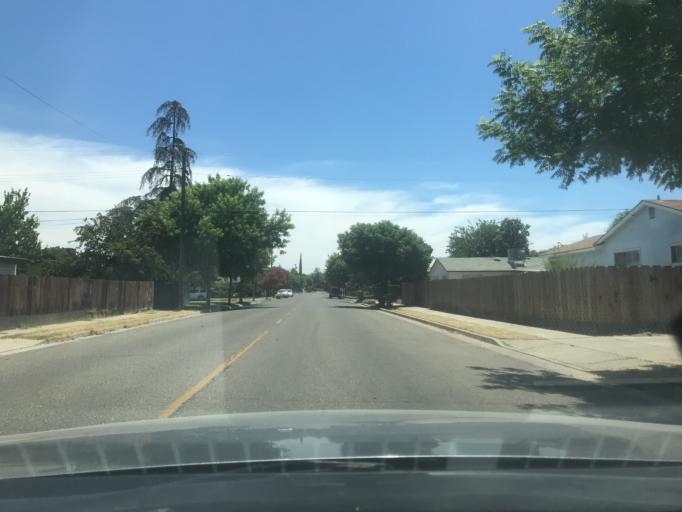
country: US
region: California
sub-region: Merced County
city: Atwater
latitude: 37.3594
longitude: -120.6070
